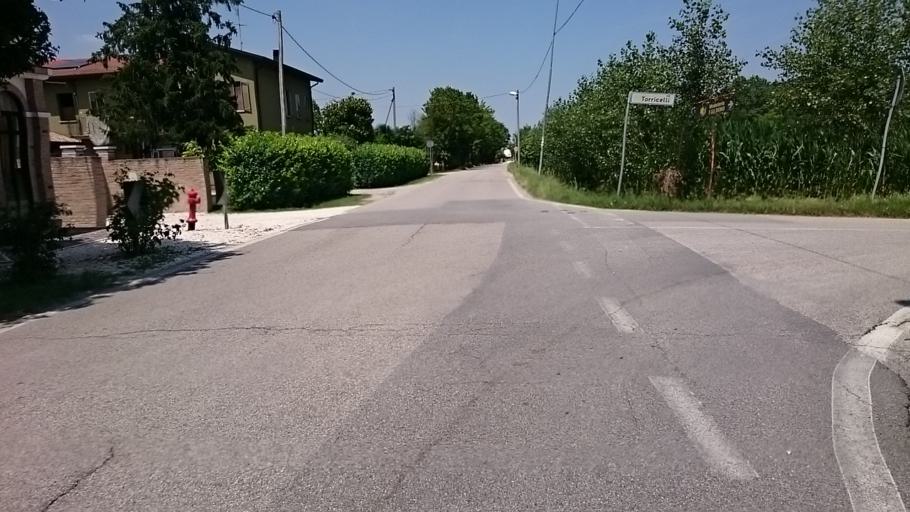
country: IT
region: Veneto
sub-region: Provincia di Padova
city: Pionca
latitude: 45.4750
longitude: 11.9720
